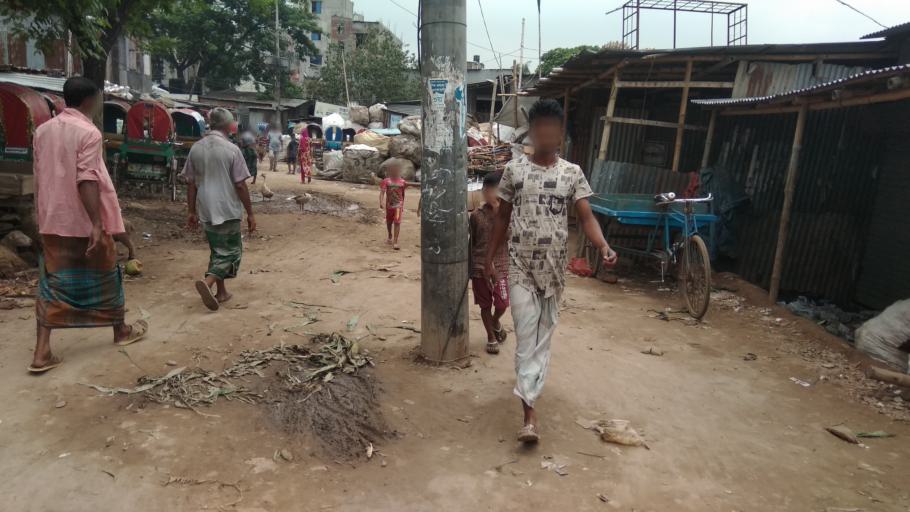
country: BD
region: Dhaka
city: Tungi
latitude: 23.8217
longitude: 90.3804
